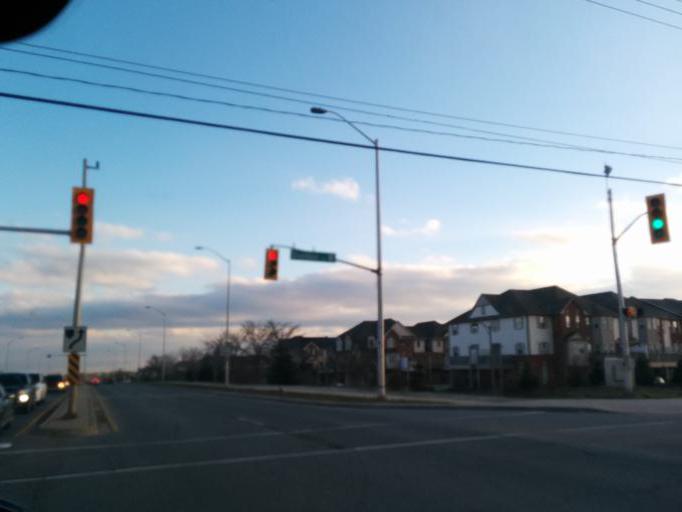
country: CA
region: Ontario
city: Burlington
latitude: 43.4346
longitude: -79.7774
